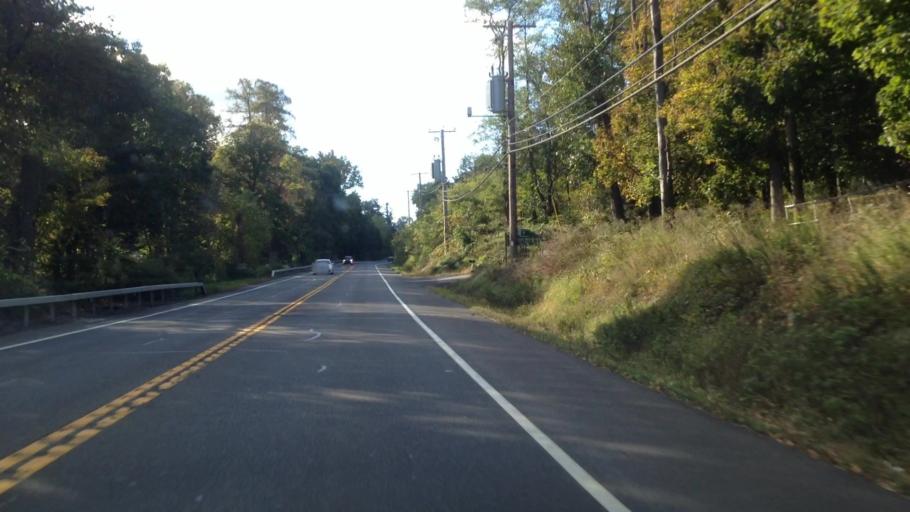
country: US
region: New York
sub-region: Dutchess County
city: Hyde Park
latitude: 41.7871
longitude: -73.9596
